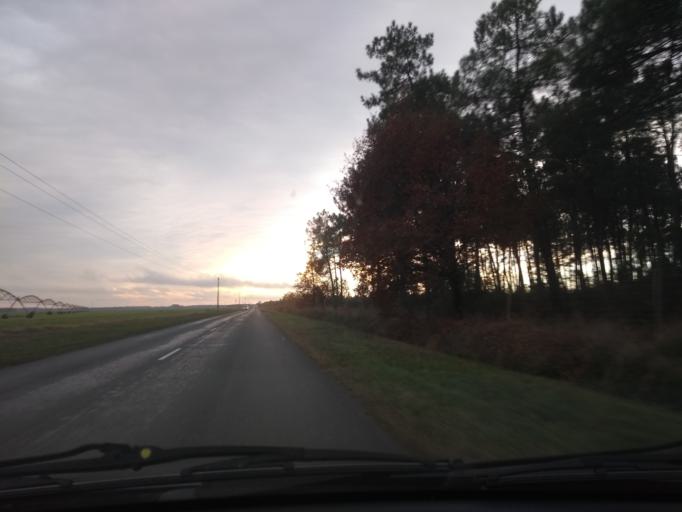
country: FR
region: Aquitaine
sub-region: Departement de la Gironde
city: Saucats
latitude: 44.6310
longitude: -0.6563
